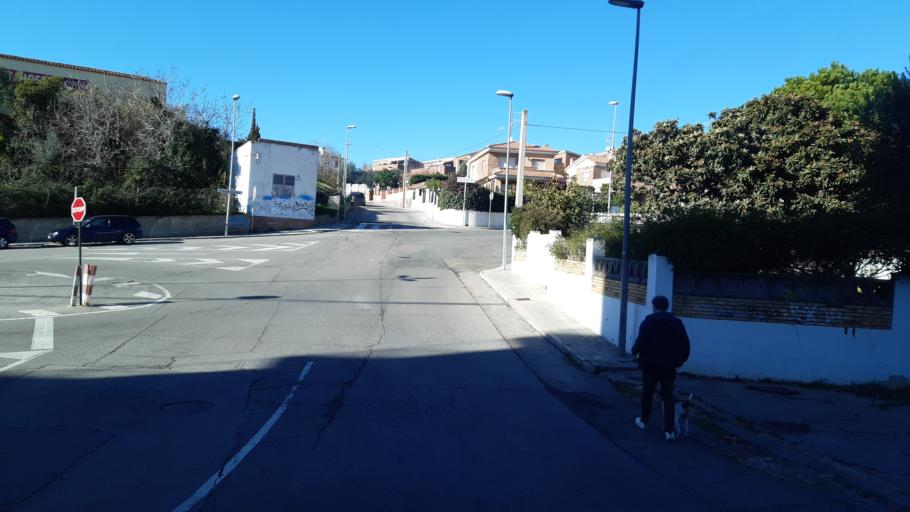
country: ES
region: Catalonia
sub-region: Provincia de Tarragona
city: Cunit
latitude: 41.1991
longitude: 1.6336
